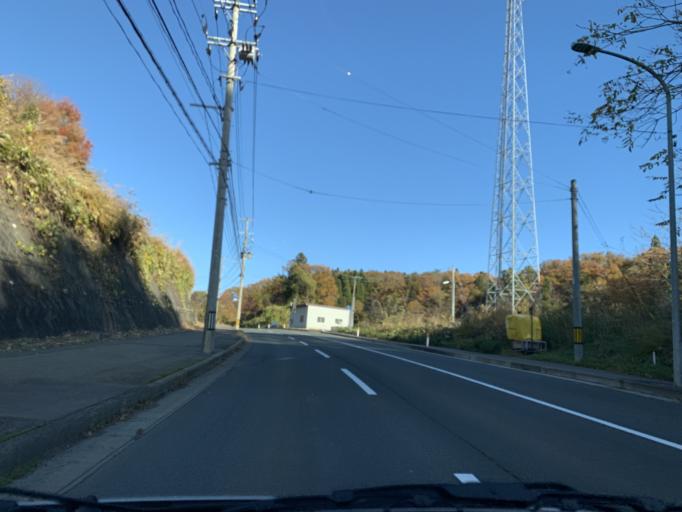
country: JP
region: Iwate
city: Mizusawa
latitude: 39.2016
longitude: 141.1747
